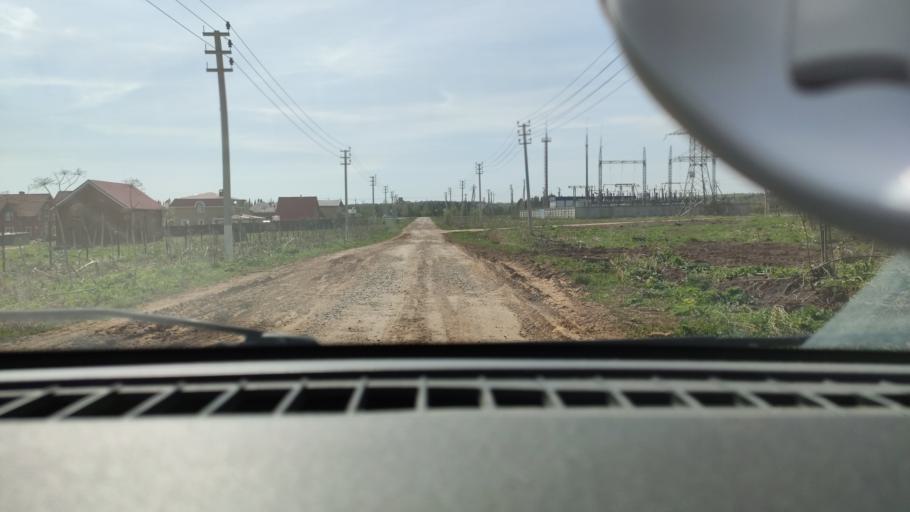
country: RU
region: Perm
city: Kultayevo
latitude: 57.8824
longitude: 55.8486
